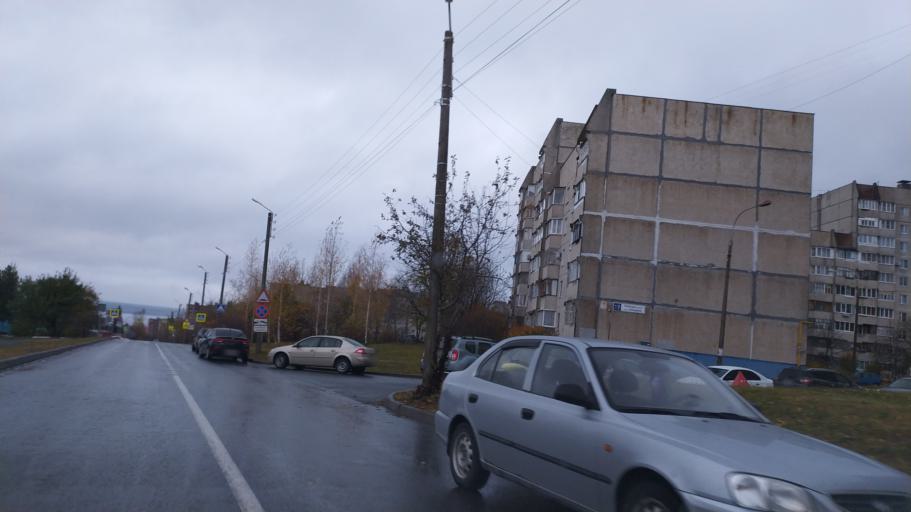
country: RU
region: Chuvashia
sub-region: Cheboksarskiy Rayon
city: Cheboksary
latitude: 56.1445
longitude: 47.1615
